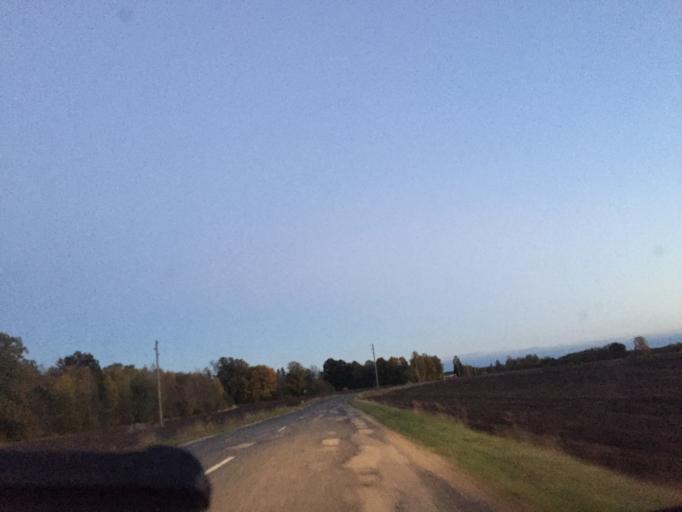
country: LV
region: Talsu Rajons
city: Sabile
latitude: 56.9657
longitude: 22.6072
